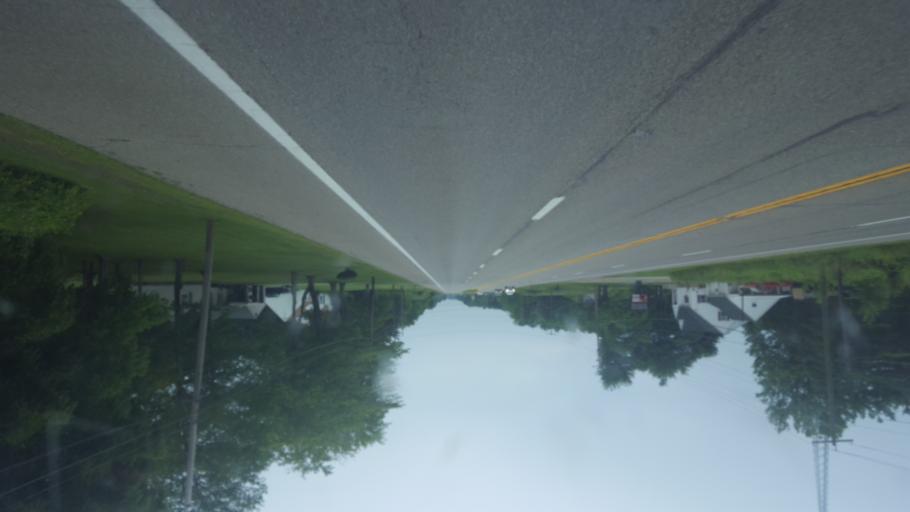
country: US
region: Ohio
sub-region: Trumbull County
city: Leavittsburg
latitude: 41.2254
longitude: -80.9180
